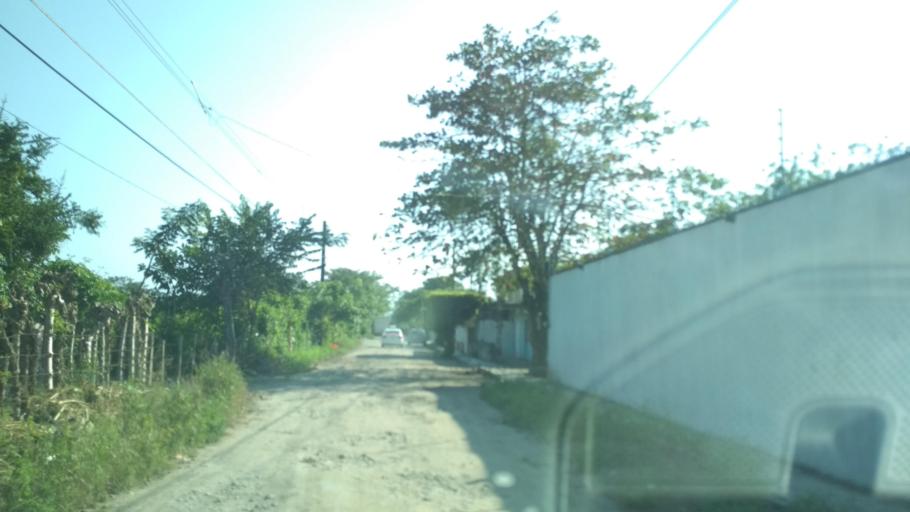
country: MX
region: Veracruz
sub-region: Martinez de la Torre
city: El Progreso
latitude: 20.0837
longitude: -97.0220
